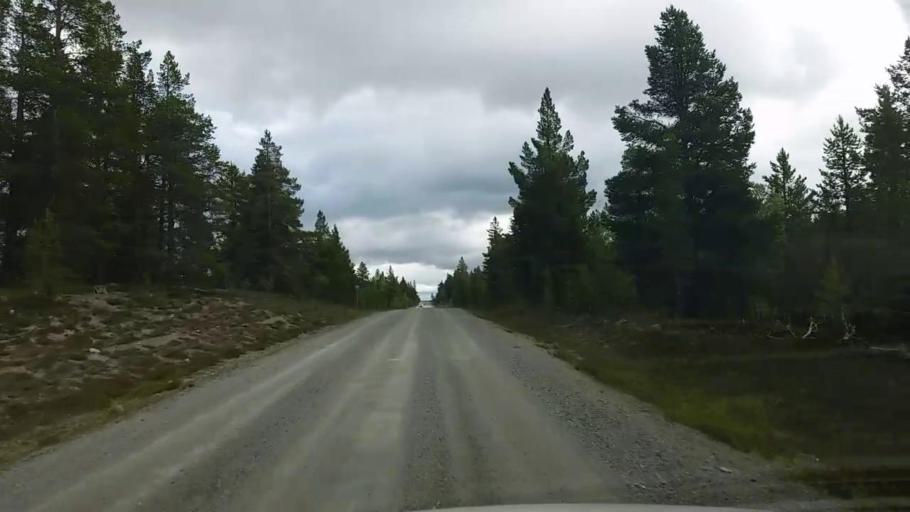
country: NO
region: Hedmark
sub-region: Engerdal
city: Engerdal
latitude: 62.3374
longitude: 12.6232
